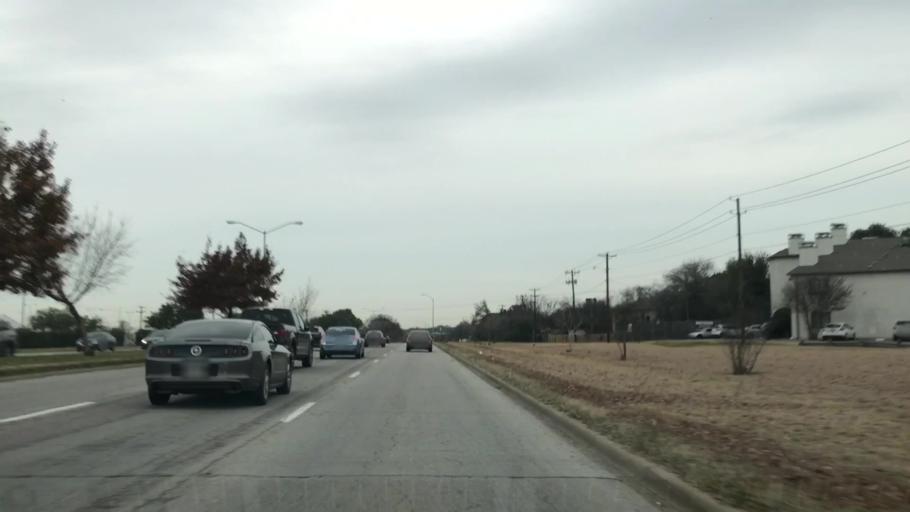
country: US
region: Texas
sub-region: Dallas County
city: University Park
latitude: 32.8523
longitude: -96.8429
